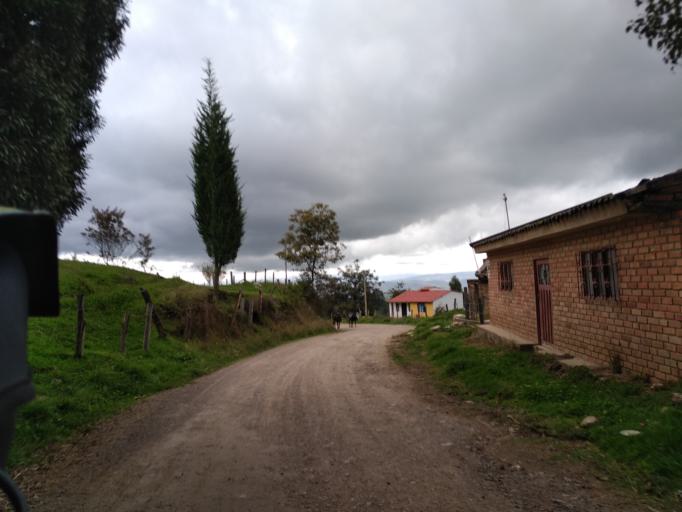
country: CO
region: Boyaca
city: Sotaquira
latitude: 5.7572
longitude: -73.2884
